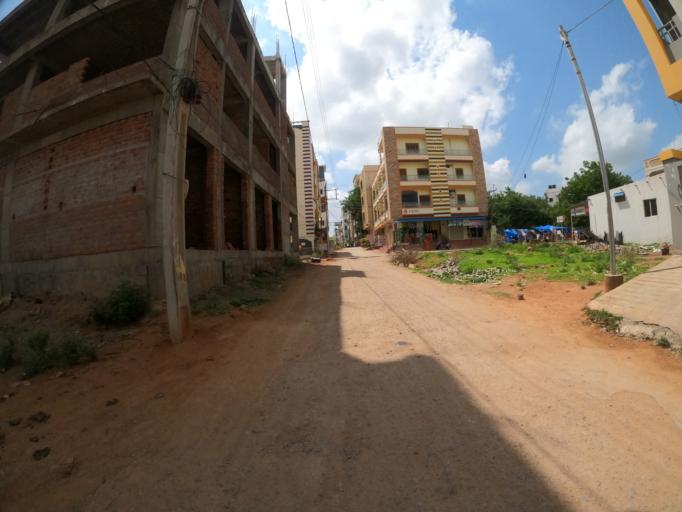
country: IN
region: Telangana
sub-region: Hyderabad
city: Hyderabad
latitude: 17.3626
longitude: 78.3861
